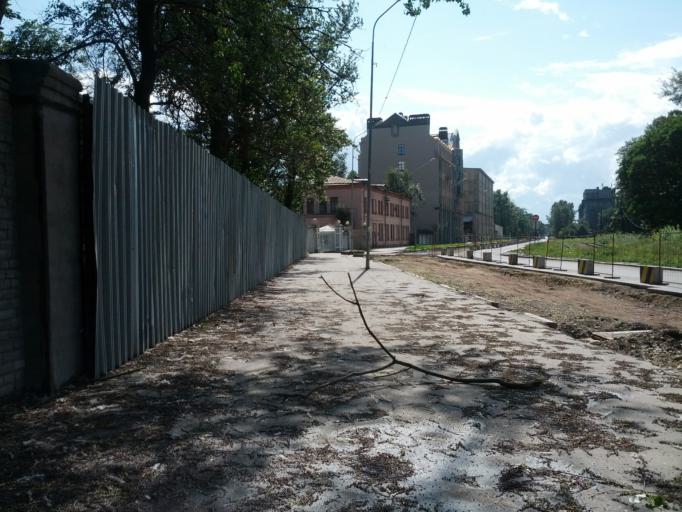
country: RU
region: St.-Petersburg
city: Saint Petersburg
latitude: 59.8973
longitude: 30.3299
